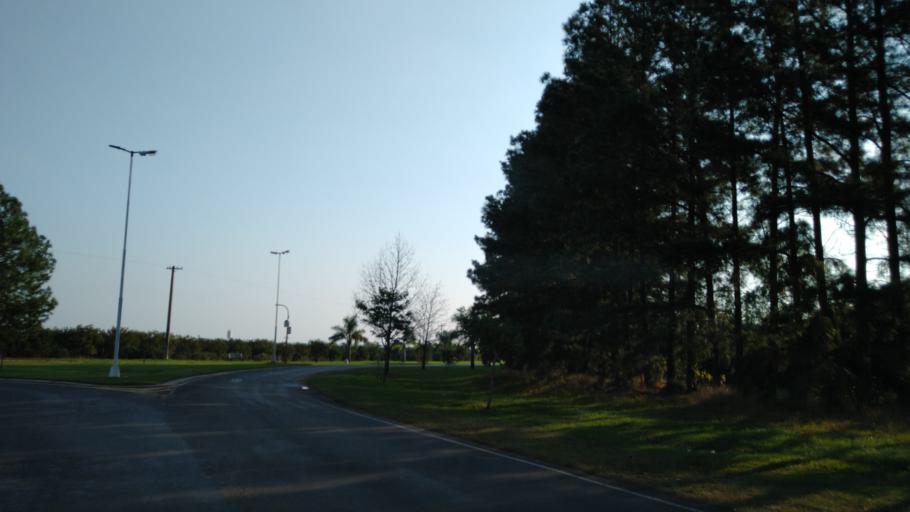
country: AR
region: Entre Rios
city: Santa Ana
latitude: -30.8997
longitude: -57.9243
